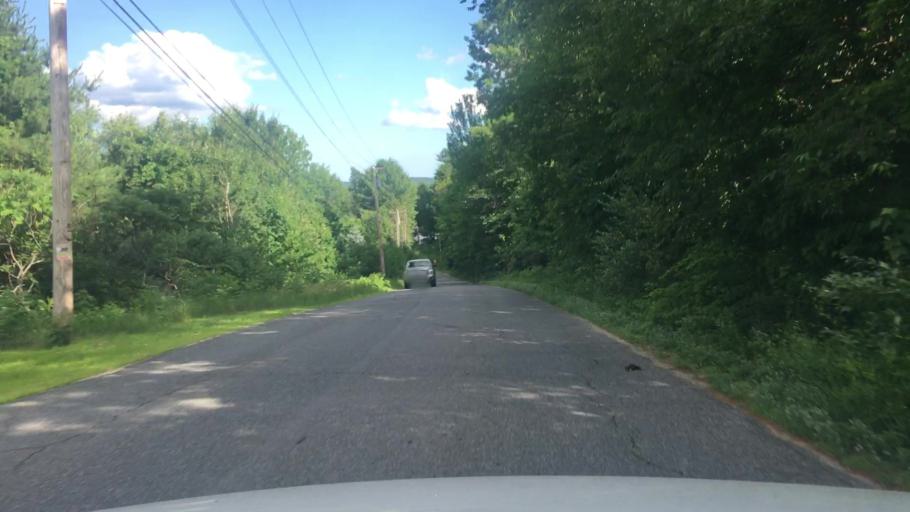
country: US
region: Maine
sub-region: Franklin County
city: Wilton
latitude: 44.6023
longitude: -70.2246
